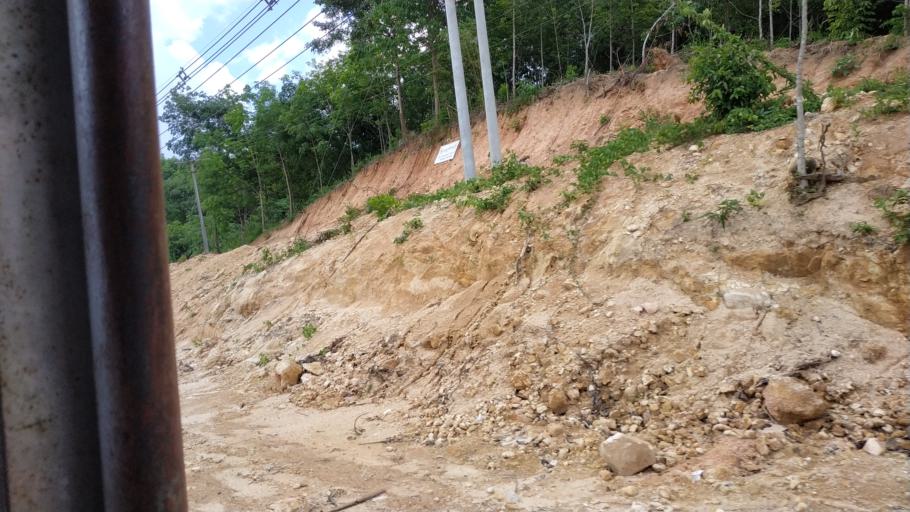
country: MM
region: Mon
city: Kyaikto
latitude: 17.4180
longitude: 97.0710
